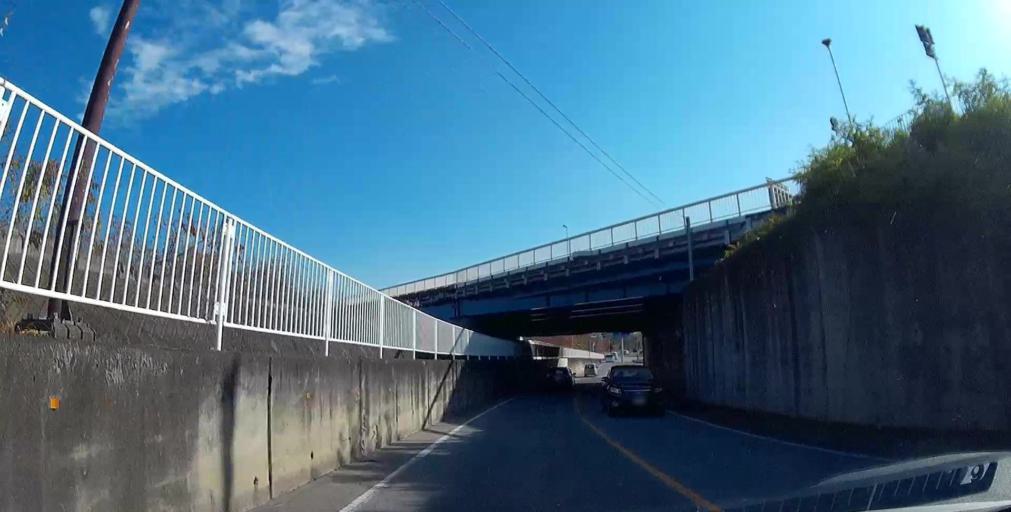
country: JP
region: Yamanashi
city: Isawa
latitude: 35.6465
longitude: 138.6676
